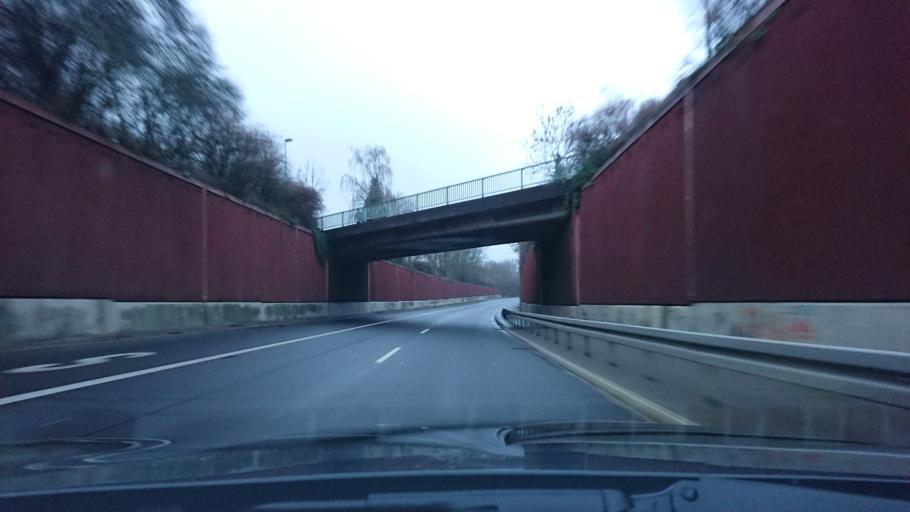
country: DE
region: North Rhine-Westphalia
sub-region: Regierungsbezirk Koln
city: Bonn
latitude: 50.7737
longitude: 7.0839
